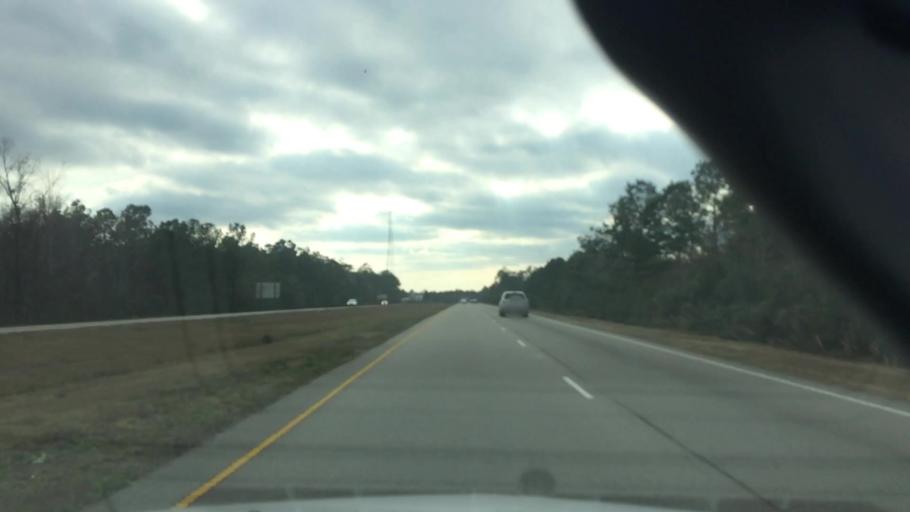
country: US
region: North Carolina
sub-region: Brunswick County
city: Shallotte
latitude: 33.9695
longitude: -78.4120
